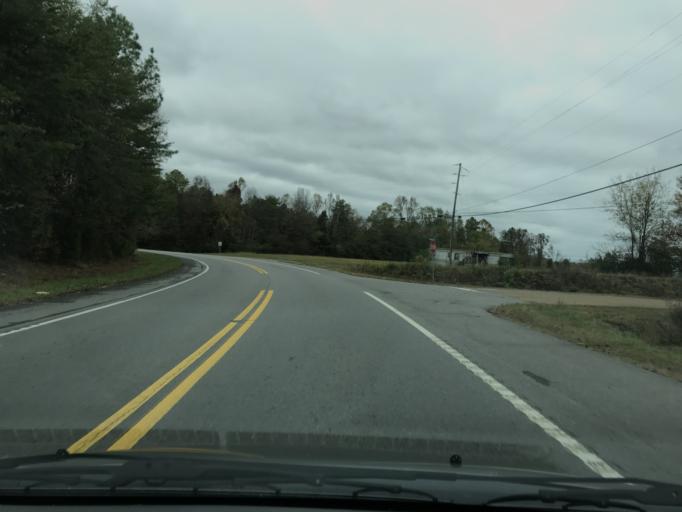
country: US
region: Tennessee
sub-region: Hamilton County
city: Sale Creek
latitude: 35.3663
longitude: -84.9904
